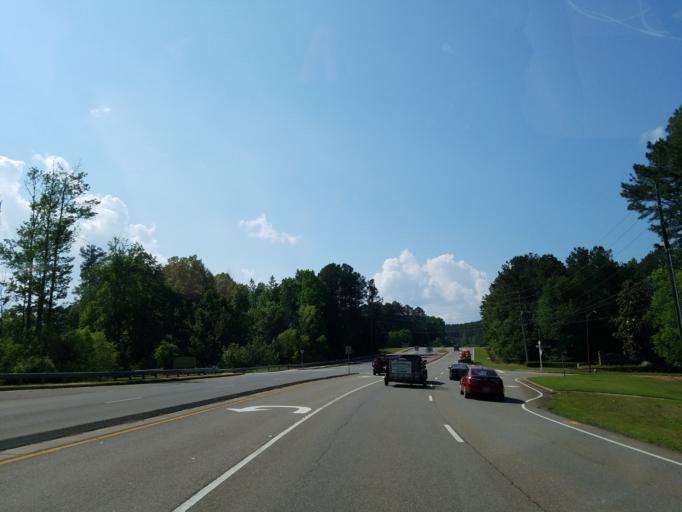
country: US
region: Georgia
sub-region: Cherokee County
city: Holly Springs
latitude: 34.1616
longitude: -84.5373
